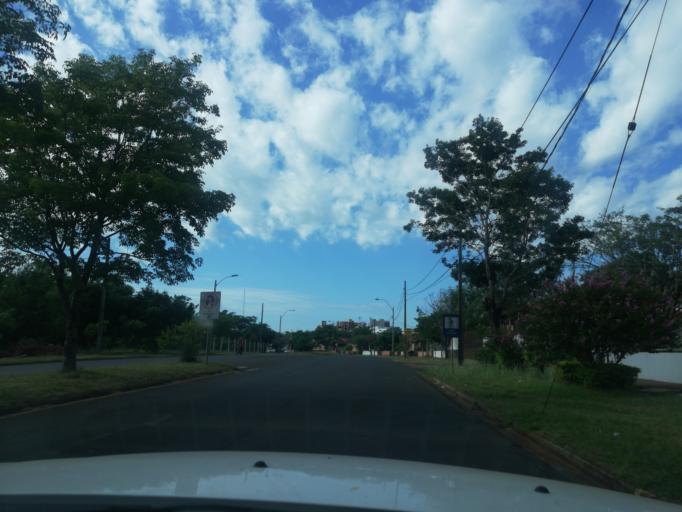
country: PY
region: Itapua
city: Encarnacion
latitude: -27.3528
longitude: -55.8491
